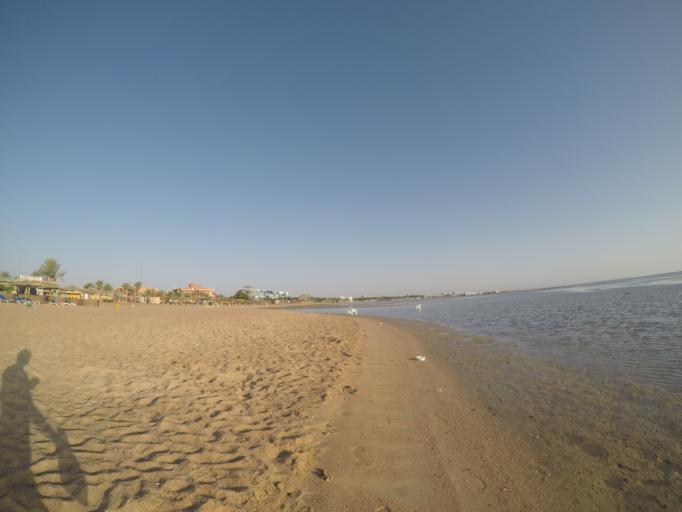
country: EG
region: Red Sea
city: Makadi Bay
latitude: 27.0927
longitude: 33.8525
